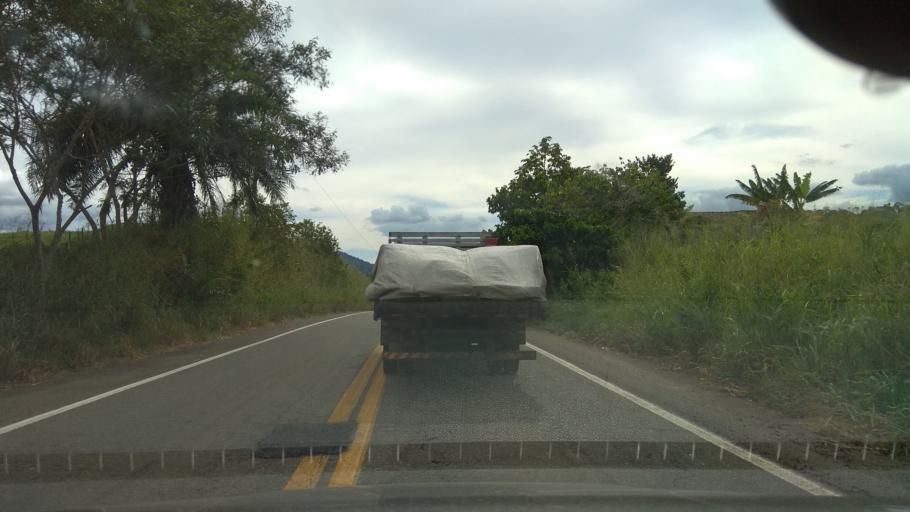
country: BR
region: Bahia
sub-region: Ipiau
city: Ipiau
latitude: -14.1924
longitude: -39.6531
